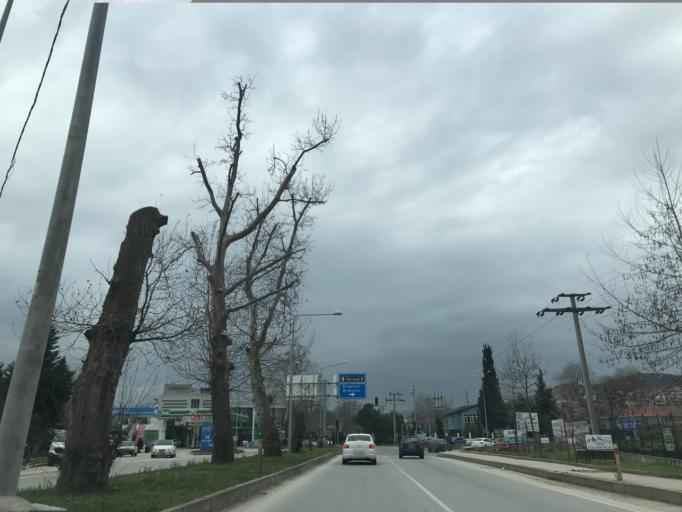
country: TR
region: Yalova
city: Kadikoy
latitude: 40.6463
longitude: 29.2342
